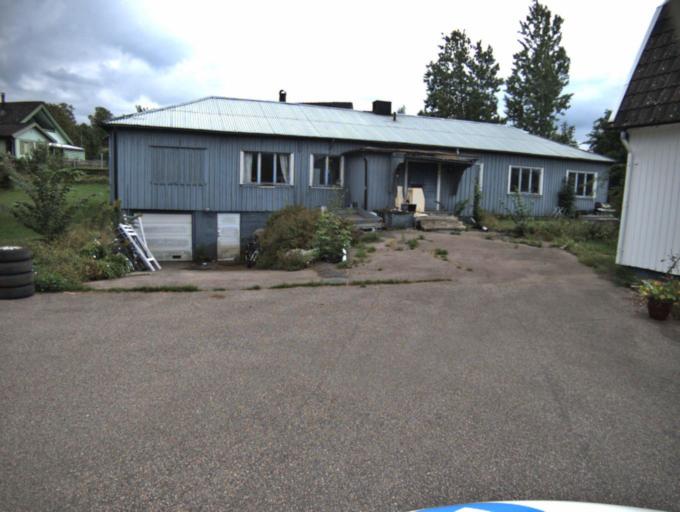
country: SE
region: Vaestra Goetaland
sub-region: Ulricehamns Kommun
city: Ulricehamn
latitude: 57.8402
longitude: 13.2842
